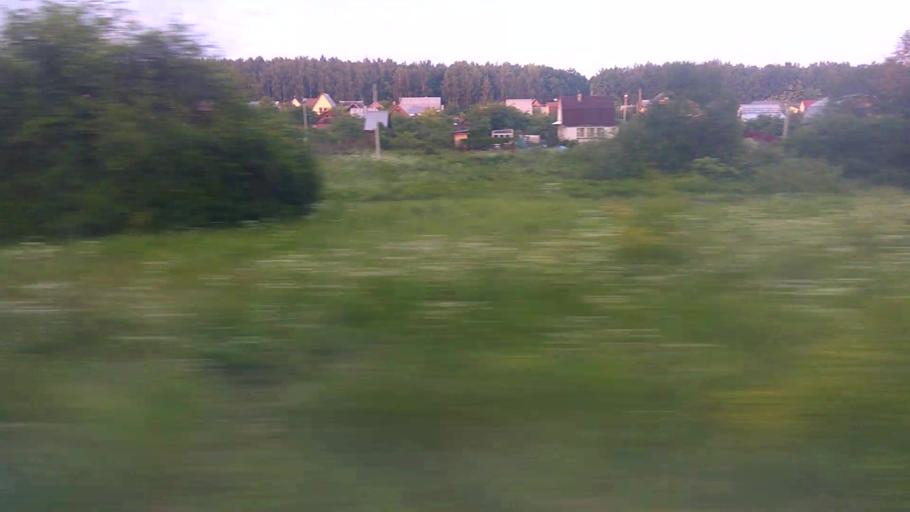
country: RU
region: Moskovskaya
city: Mikhnevo
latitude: 55.1774
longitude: 37.9331
